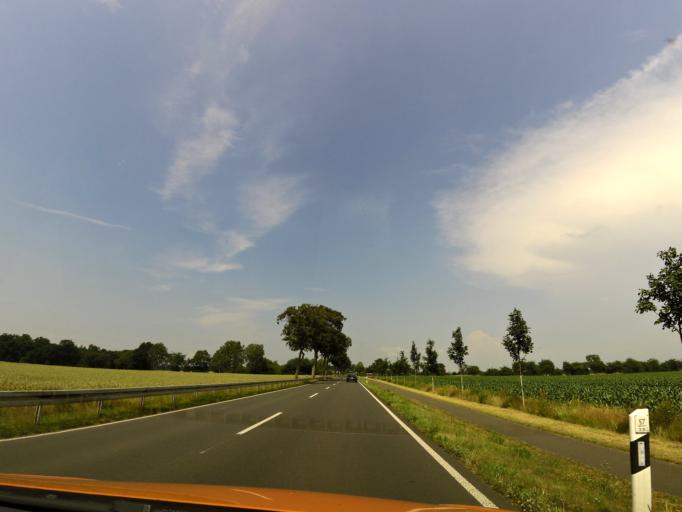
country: DE
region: Brandenburg
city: Pritzwalk
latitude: 53.1859
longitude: 12.1942
